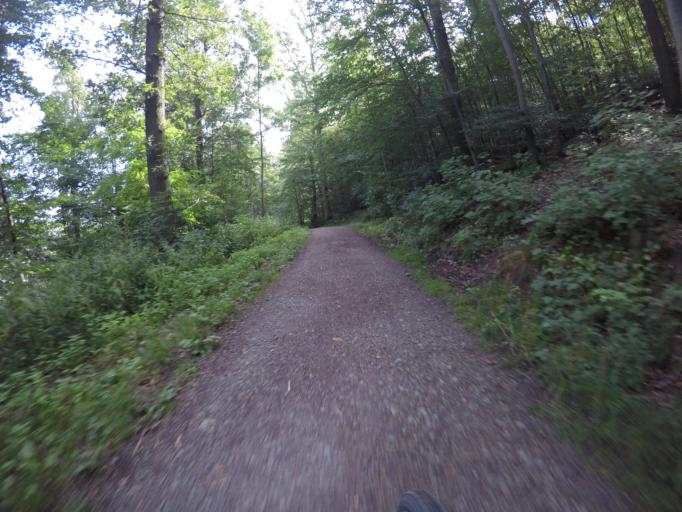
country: DE
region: Baden-Wuerttemberg
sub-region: Regierungsbezirk Stuttgart
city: Stuttgart
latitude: 48.7558
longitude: 9.1497
